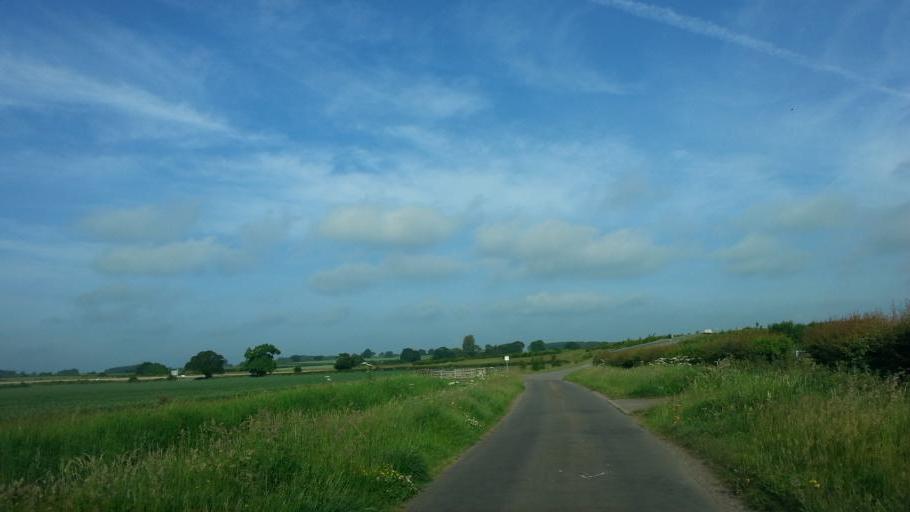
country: GB
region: England
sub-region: Nottinghamshire
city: Farndon
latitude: 53.0355
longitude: -0.8666
